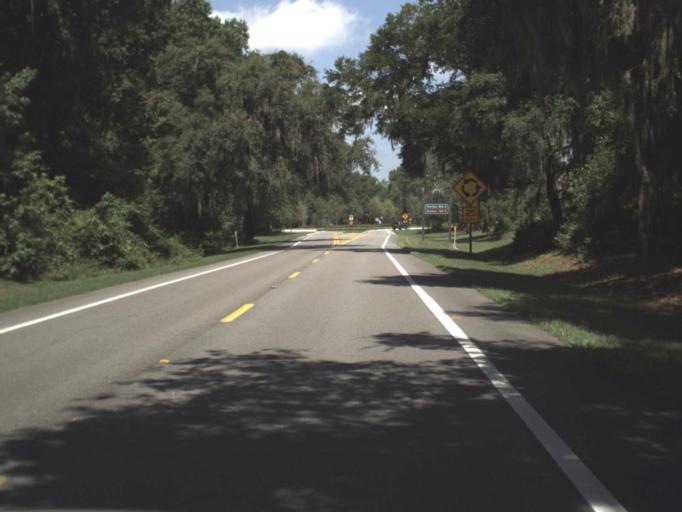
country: US
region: Florida
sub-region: Clay County
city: Green Cove Springs
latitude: 30.0194
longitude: -81.6369
